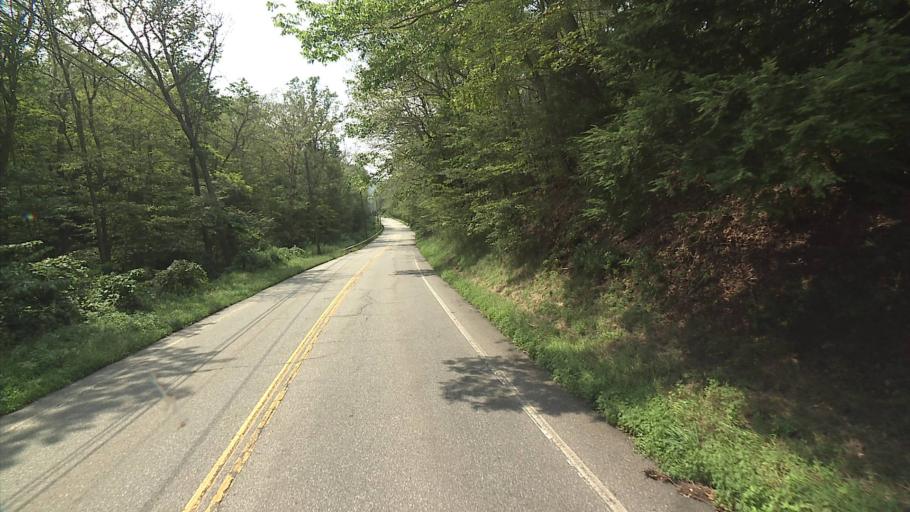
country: US
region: Connecticut
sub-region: Middlesex County
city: Essex Village
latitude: 41.4461
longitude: -72.3238
